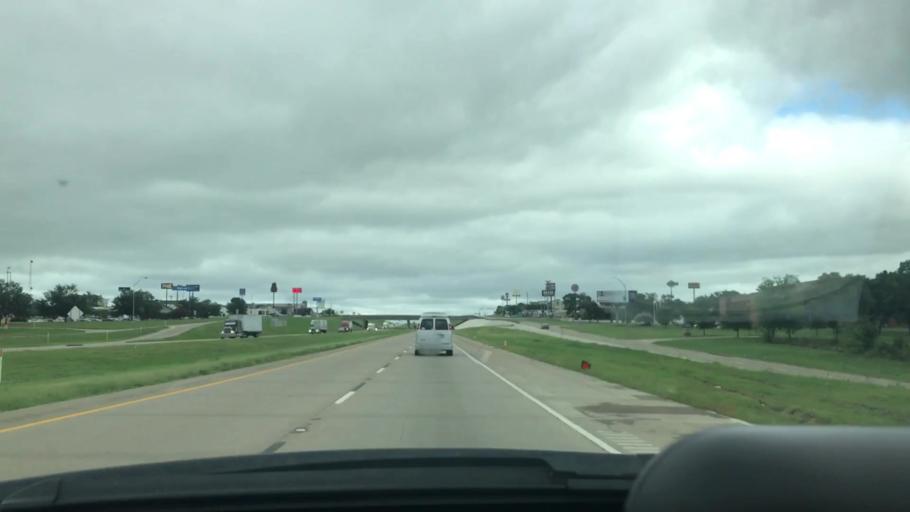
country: US
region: Texas
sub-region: Grayson County
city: Denison
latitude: 33.7569
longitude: -96.5852
